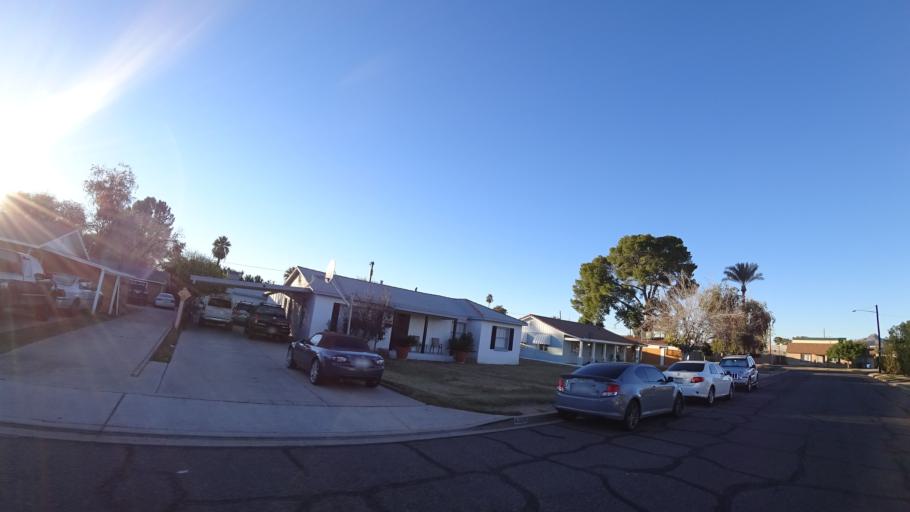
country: US
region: Arizona
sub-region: Maricopa County
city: Phoenix
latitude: 33.4787
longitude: -112.0280
